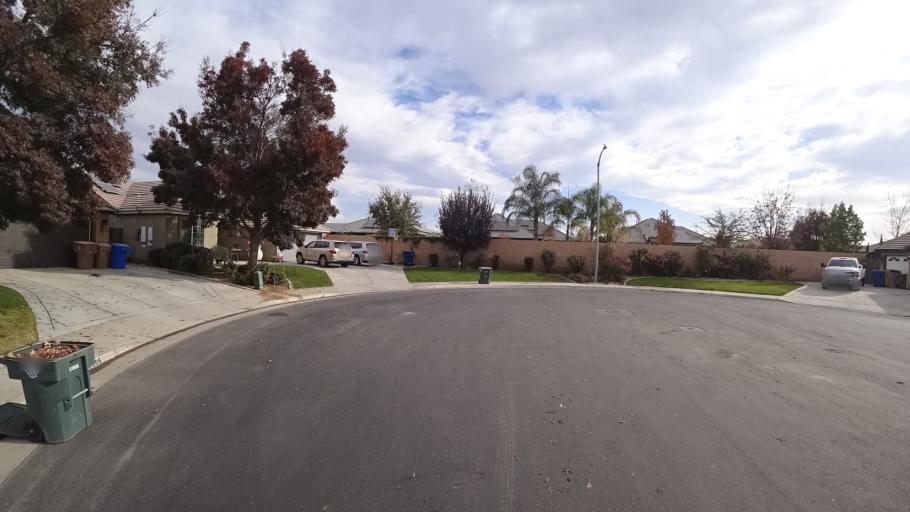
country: US
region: California
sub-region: Kern County
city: Rosedale
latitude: 35.4153
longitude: -119.1506
